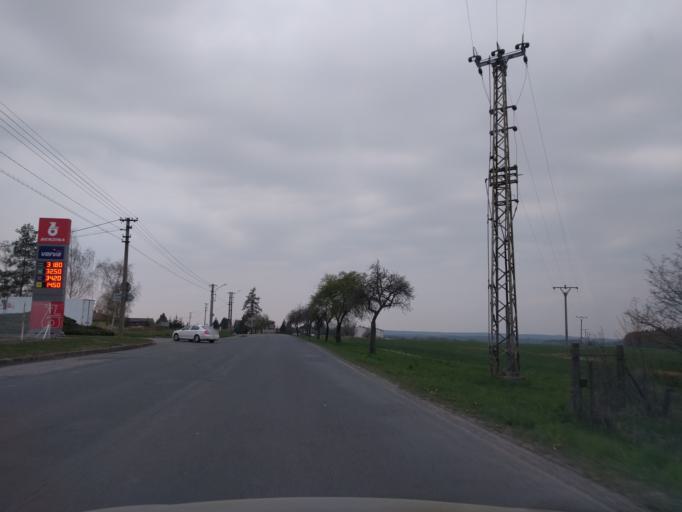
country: CZ
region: Central Bohemia
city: Kostelec nad Cernymi Lesy
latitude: 49.9930
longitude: 14.8442
